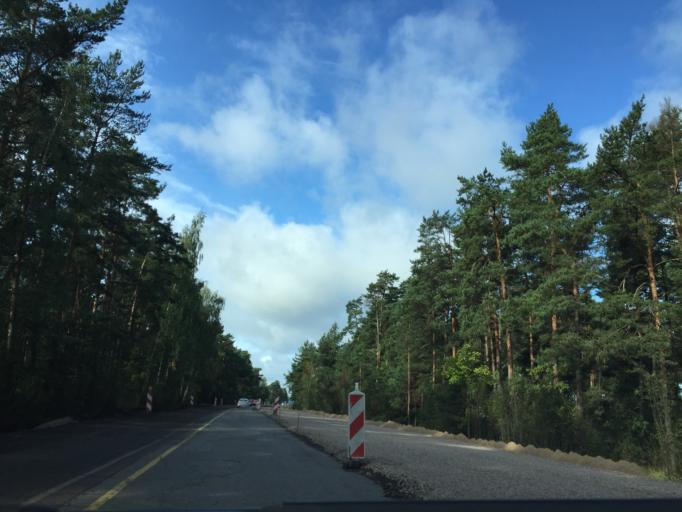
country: LV
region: Jurmala
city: Jurmala
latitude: 56.9538
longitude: 23.8190
